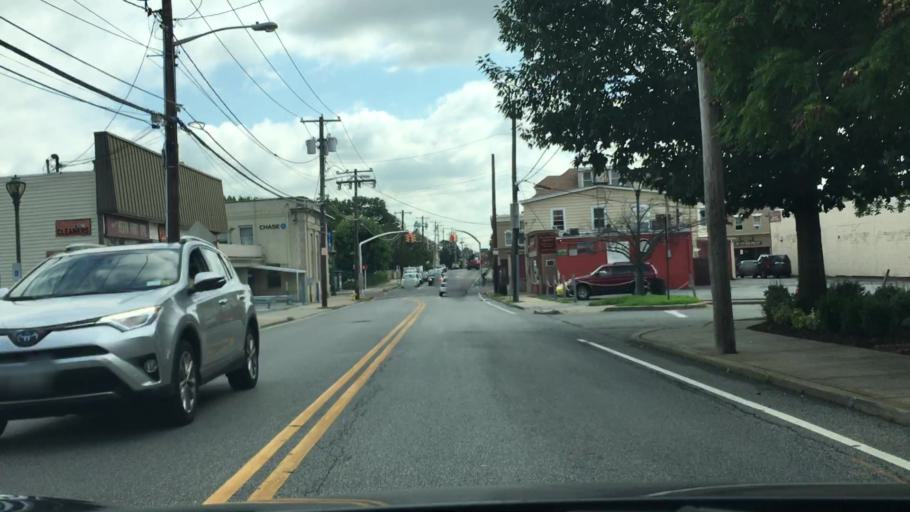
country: US
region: New York
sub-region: Nassau County
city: Westbury
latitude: 40.7556
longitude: -73.5889
